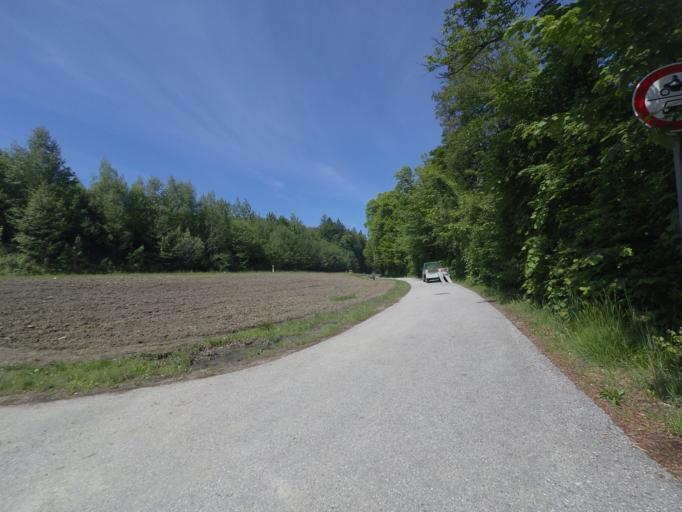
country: DE
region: Bavaria
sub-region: Upper Bavaria
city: Waging am See
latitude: 47.9326
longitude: 12.7763
